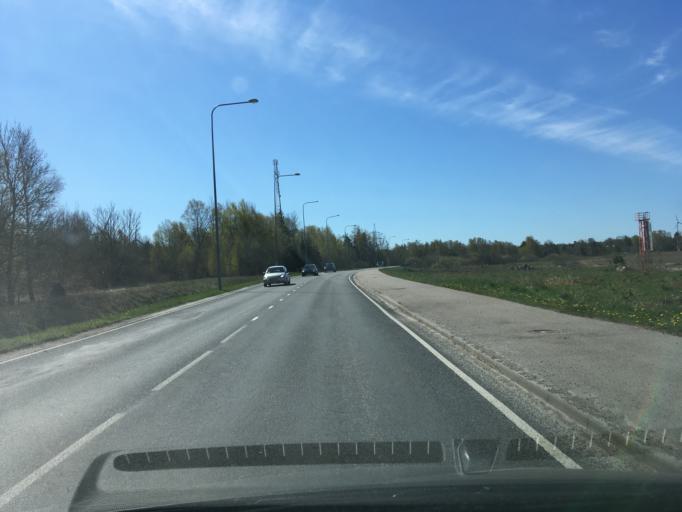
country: EE
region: Laeaene
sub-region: Lihula vald
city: Lihula
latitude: 58.5774
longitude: 23.5237
